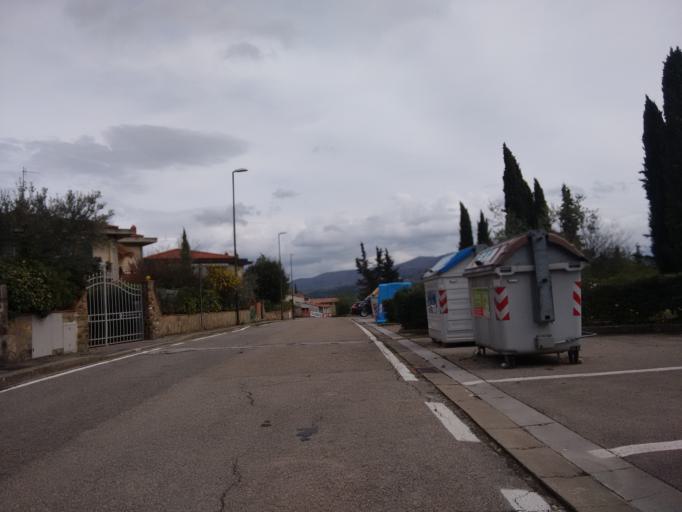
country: IT
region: Tuscany
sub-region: Province of Florence
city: Strada in Chianti
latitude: 43.6573
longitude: 11.3061
